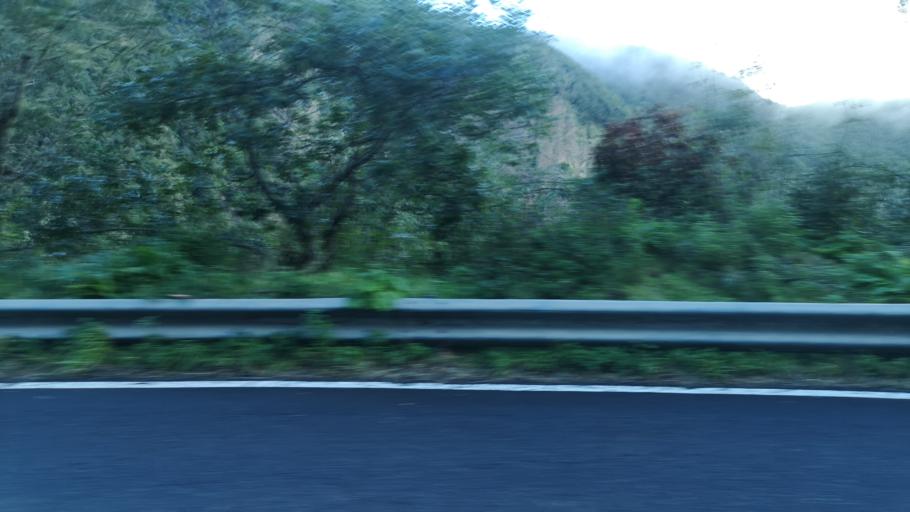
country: ES
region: Canary Islands
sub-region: Provincia de Santa Cruz de Tenerife
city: Hermigua
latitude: 28.1256
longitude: -17.2093
